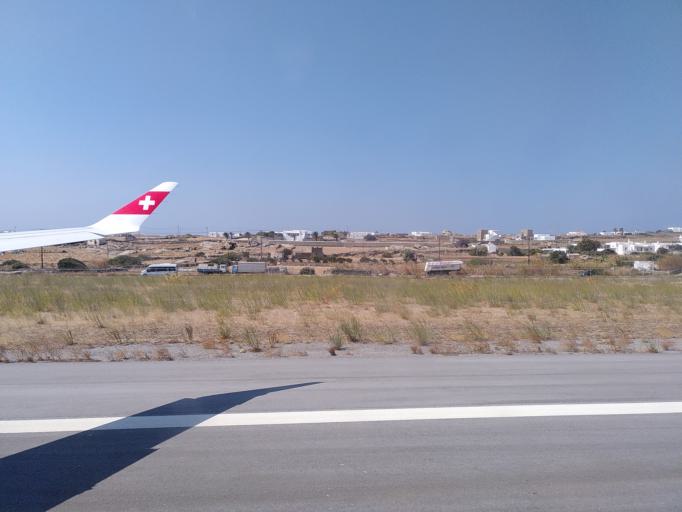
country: GR
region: South Aegean
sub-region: Nomos Kykladon
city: Mykonos
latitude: 37.4282
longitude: 25.3514
